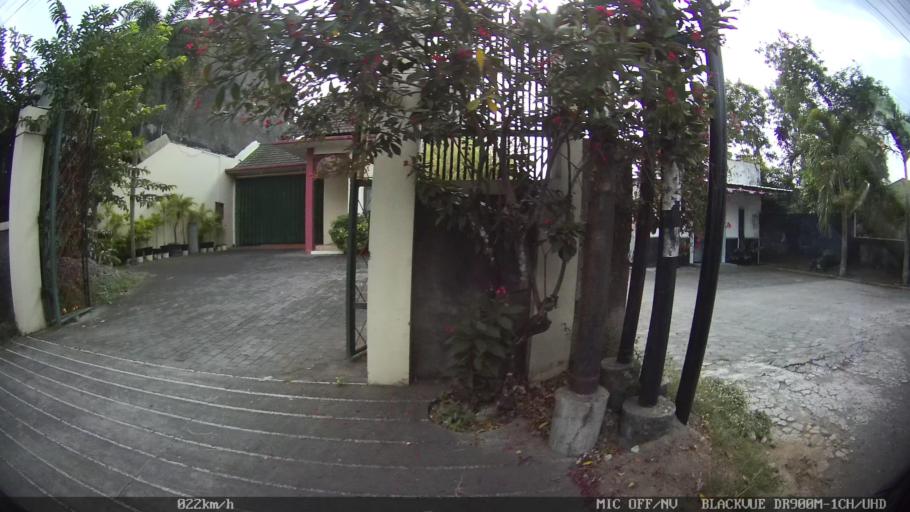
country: ID
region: Daerah Istimewa Yogyakarta
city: Melati
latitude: -7.7490
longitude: 110.3481
